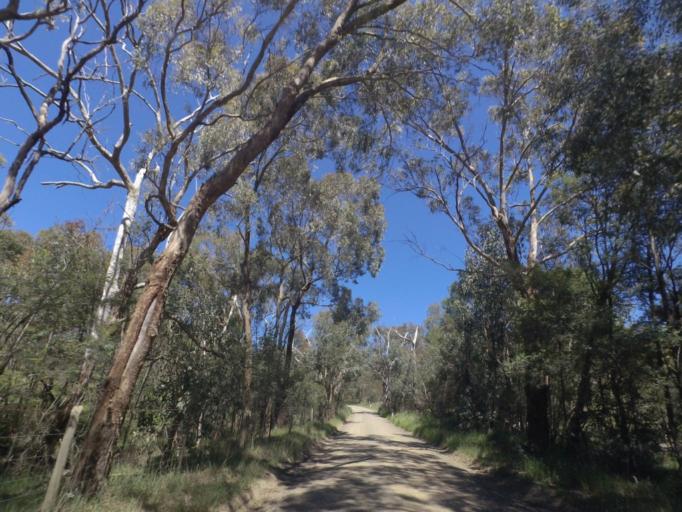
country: AU
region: Victoria
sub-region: Whittlesea
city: Whittlesea
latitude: -37.2801
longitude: 145.0128
